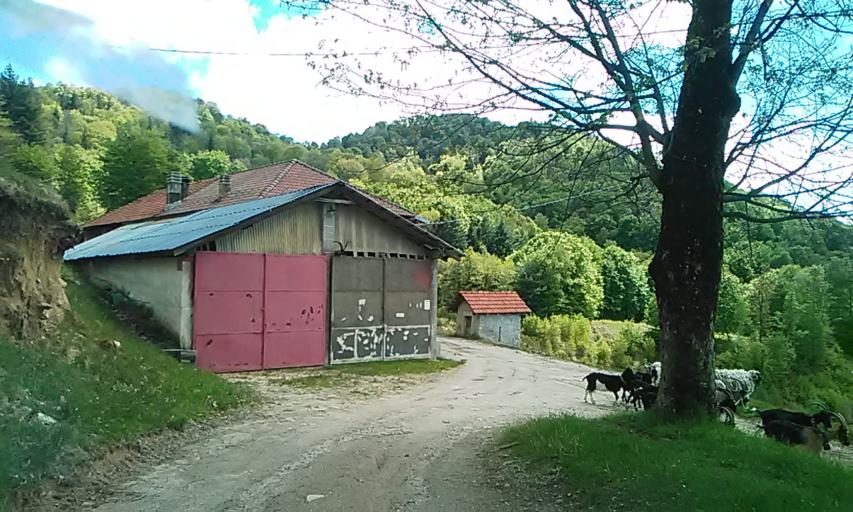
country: IT
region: Piedmont
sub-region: Provincia di Vercelli
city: Civiasco
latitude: 45.7904
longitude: 8.3041
